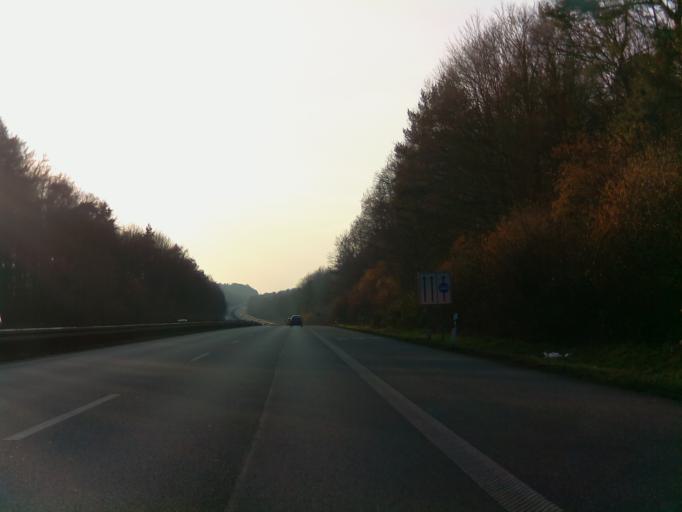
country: DE
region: Hesse
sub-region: Regierungsbezirk Darmstadt
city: Rossdorf
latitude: 49.8700
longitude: 8.7437
